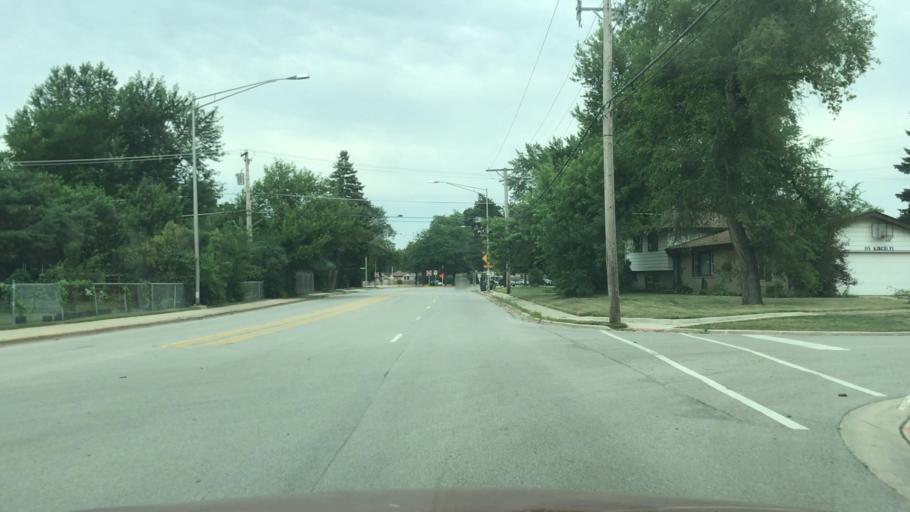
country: US
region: Illinois
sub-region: Cook County
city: Arlington Heights
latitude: 42.0675
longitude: -87.9856
